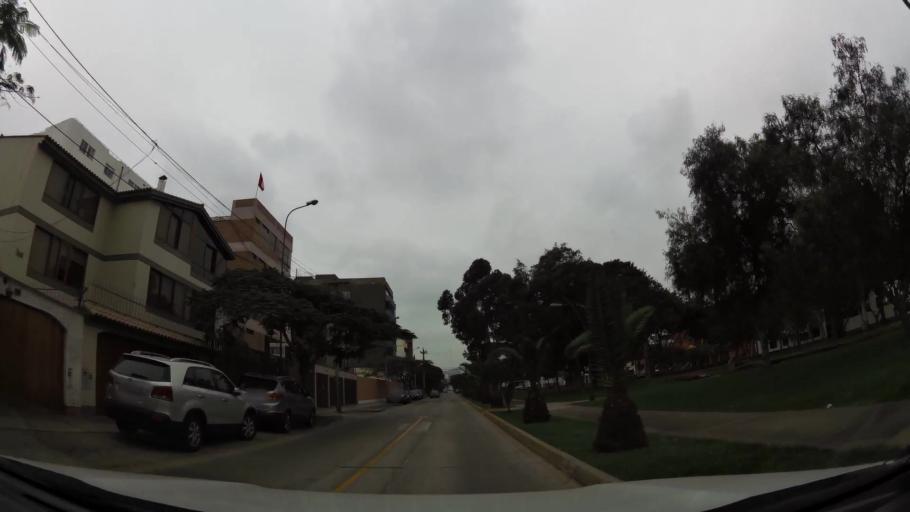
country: PE
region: Lima
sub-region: Lima
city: San Luis
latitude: -12.0931
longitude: -77.0083
